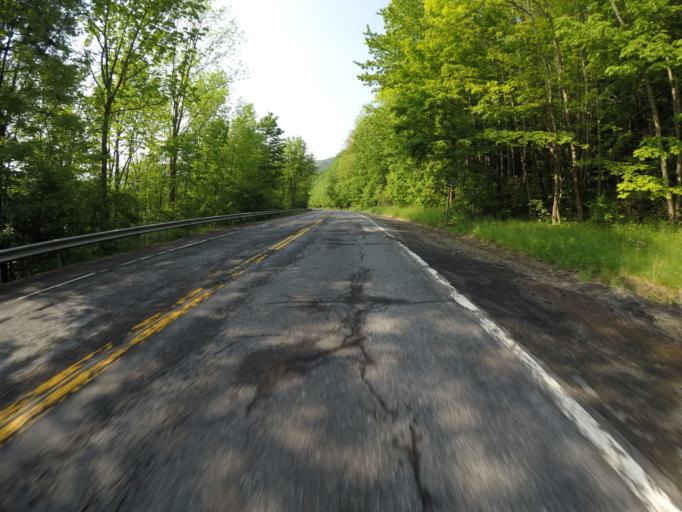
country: US
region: New York
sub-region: Sullivan County
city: Livingston Manor
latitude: 42.0953
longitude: -74.7994
